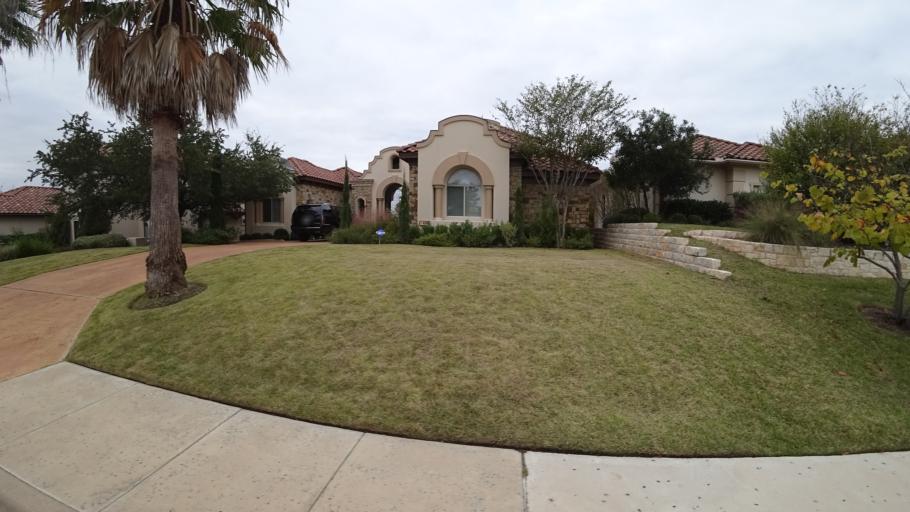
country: US
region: Texas
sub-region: Travis County
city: Bee Cave
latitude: 30.3189
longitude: -97.9176
